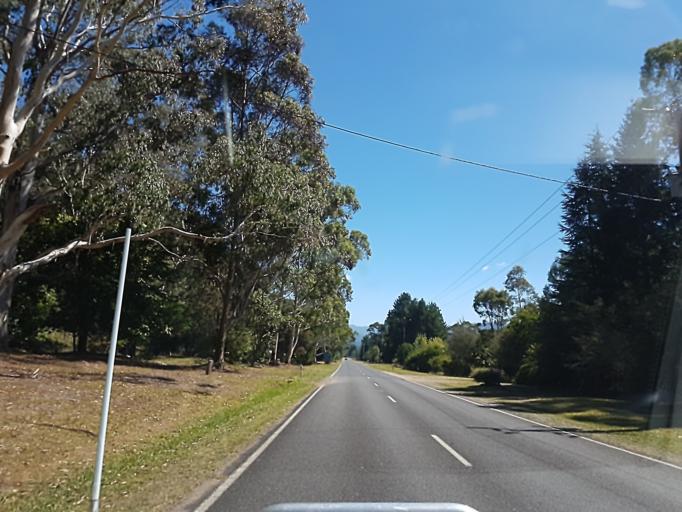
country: AU
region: Victoria
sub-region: Alpine
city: Mount Beauty
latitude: -36.7791
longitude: 147.0336
